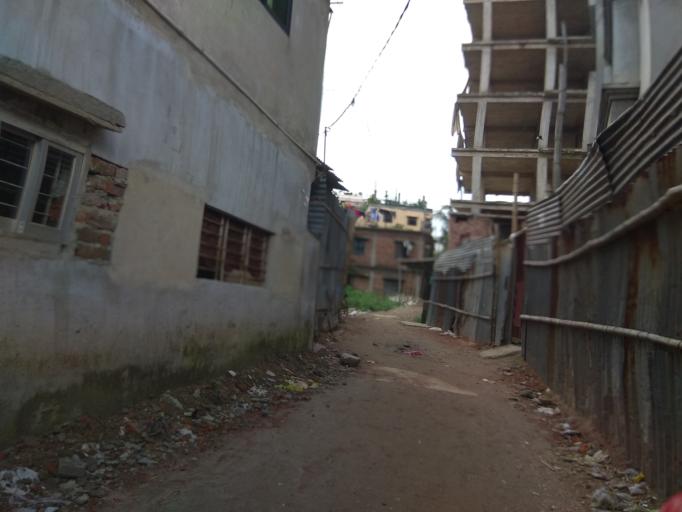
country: BD
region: Dhaka
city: Tungi
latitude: 23.8255
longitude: 90.3898
